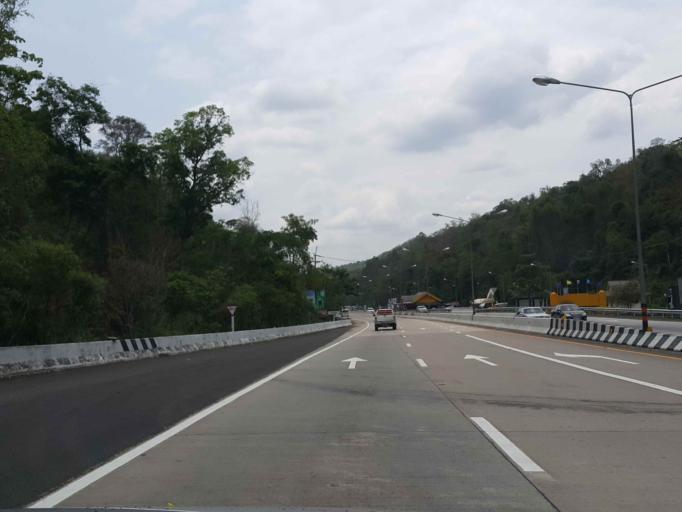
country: TH
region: Lamphun
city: Mae Tha
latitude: 18.3933
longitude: 99.2163
